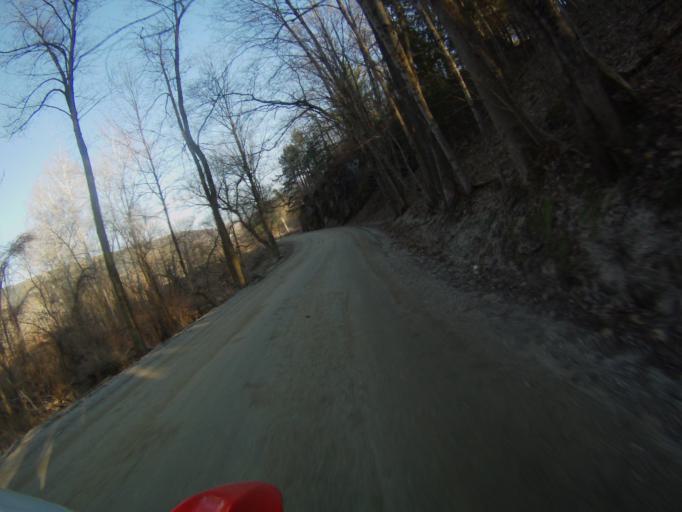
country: US
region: Vermont
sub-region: Addison County
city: Bristol
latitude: 44.0921
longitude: -73.1045
